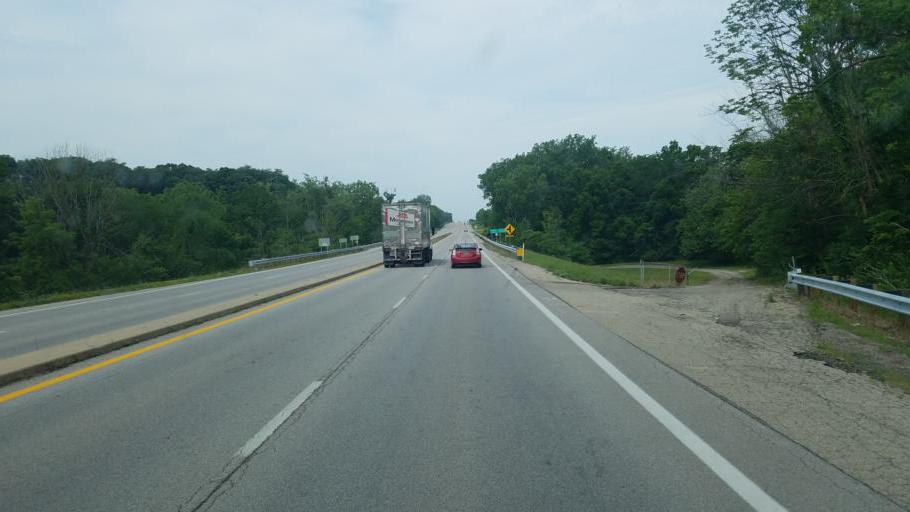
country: US
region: Ohio
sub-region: Franklin County
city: Lake Darby
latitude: 39.9477
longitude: -83.2331
